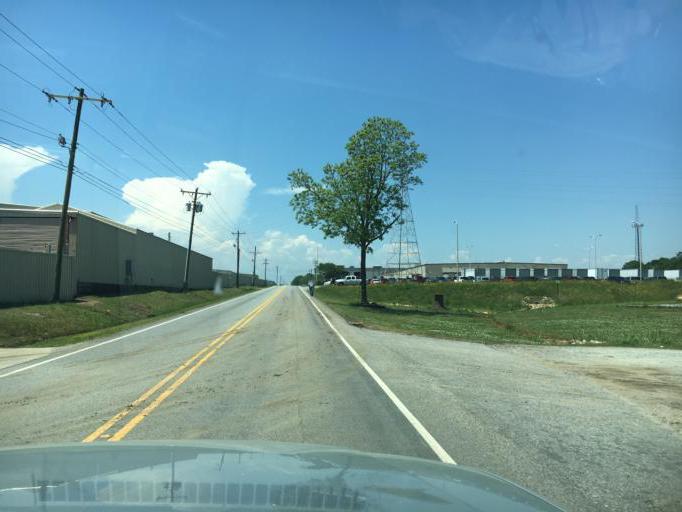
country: US
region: South Carolina
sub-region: Spartanburg County
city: Saxon
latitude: 34.9727
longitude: -81.9668
